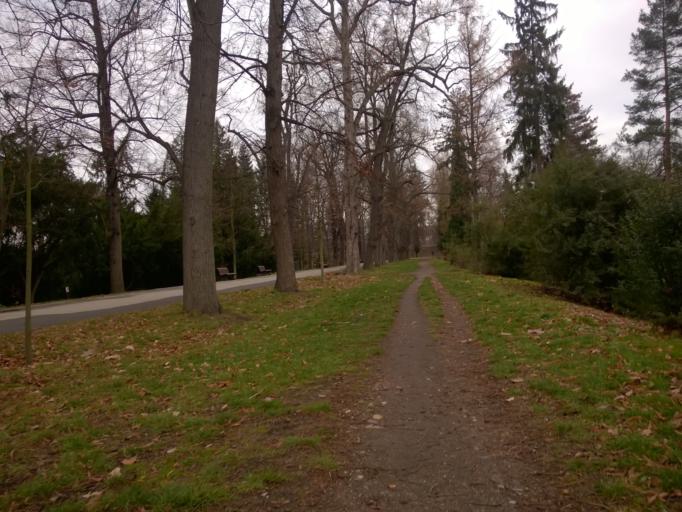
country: CZ
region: Praha
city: Prague
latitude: 50.1062
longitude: 14.4155
